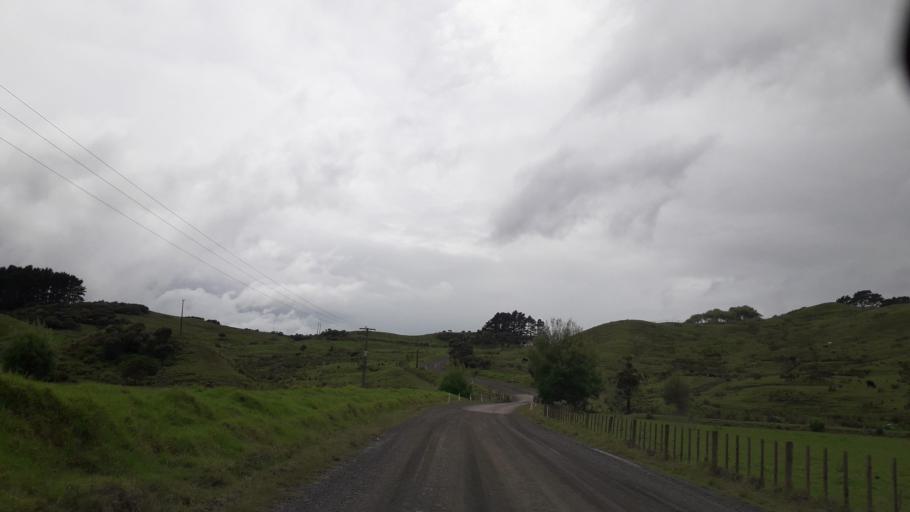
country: NZ
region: Northland
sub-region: Far North District
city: Kaitaia
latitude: -35.4174
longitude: 173.3634
